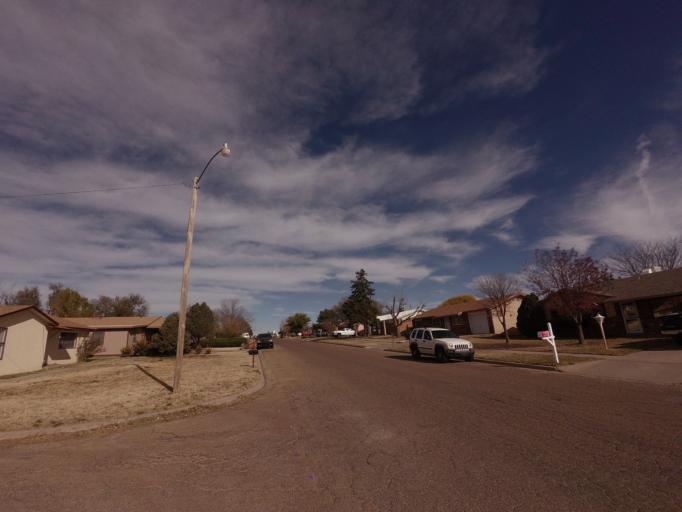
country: US
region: New Mexico
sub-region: Curry County
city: Clovis
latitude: 34.4141
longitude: -103.1953
